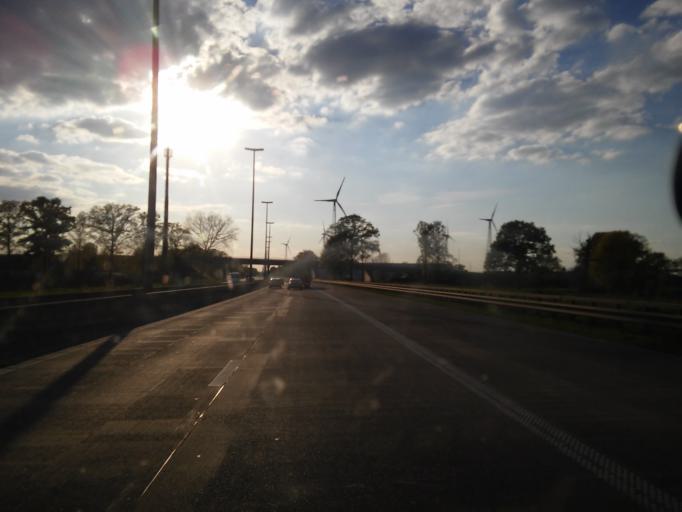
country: BE
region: Flanders
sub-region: Provincie Limburg
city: Tessenderlo
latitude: 51.0921
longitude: 5.1088
